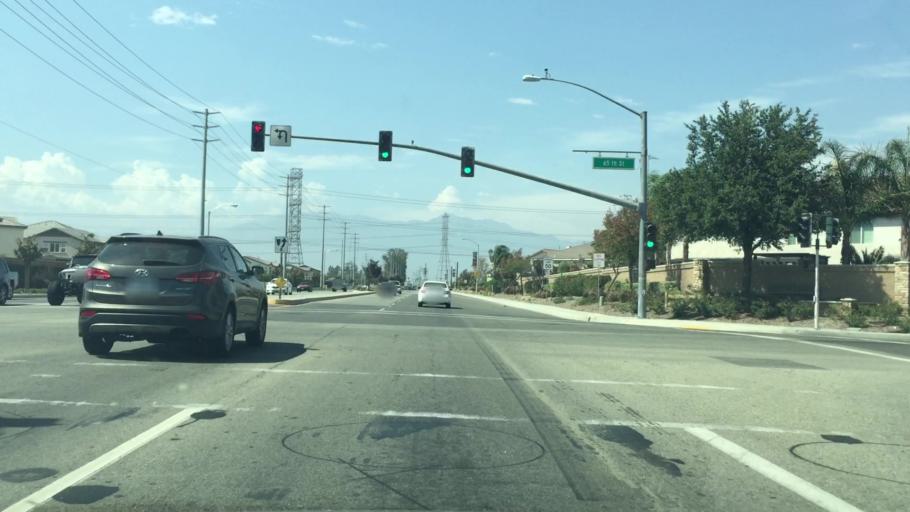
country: US
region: California
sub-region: Riverside County
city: Norco
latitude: 33.9680
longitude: -117.5931
